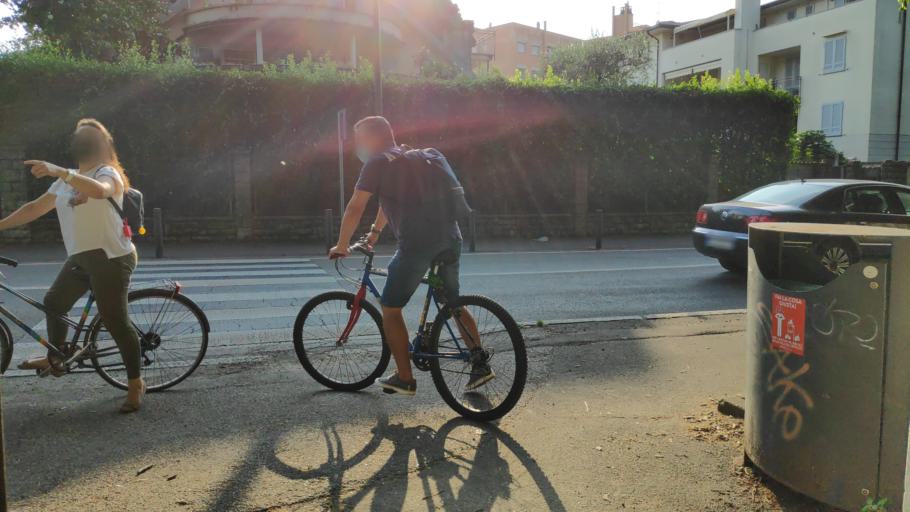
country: IT
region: Lombardy
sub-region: Citta metropolitana di Milano
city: Cernusco sul Naviglio
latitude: 45.5220
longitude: 9.3270
